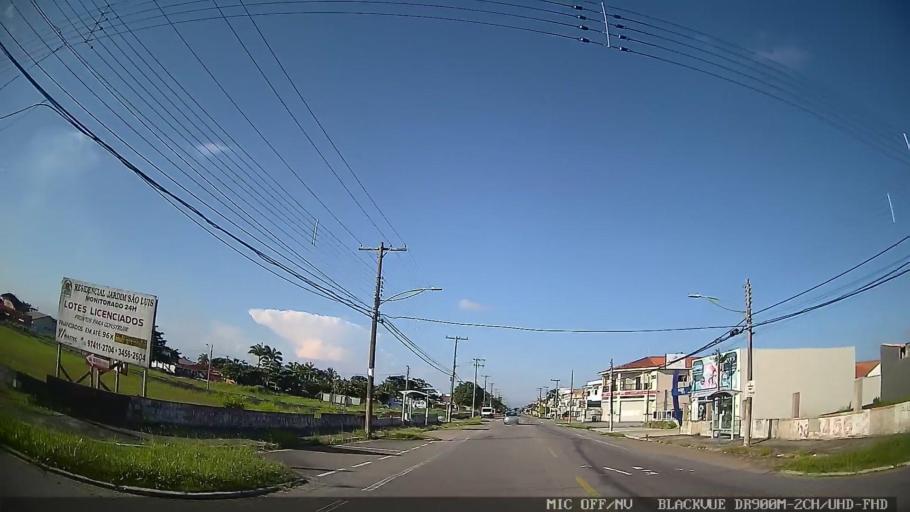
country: BR
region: Sao Paulo
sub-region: Peruibe
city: Peruibe
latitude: -24.2892
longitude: -46.9606
